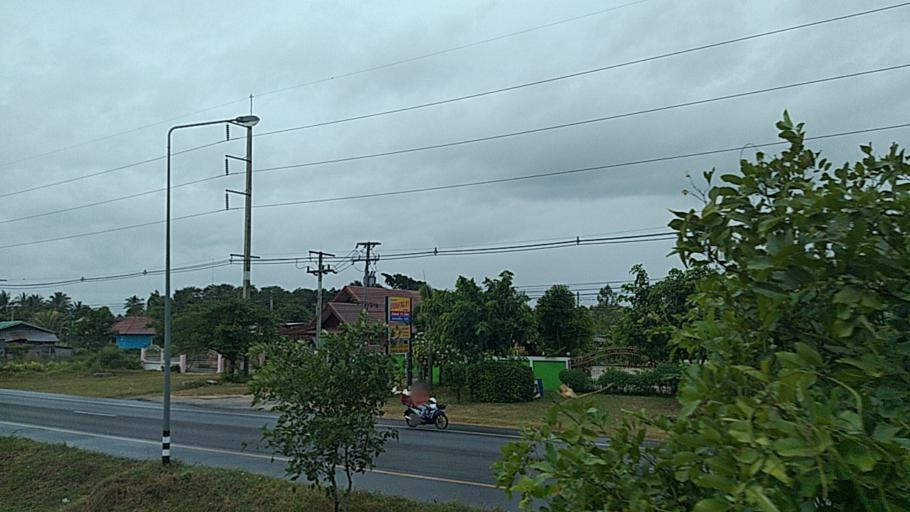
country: TH
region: Maha Sarakham
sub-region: Amphoe Borabue
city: Borabue
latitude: 16.0578
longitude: 103.1356
